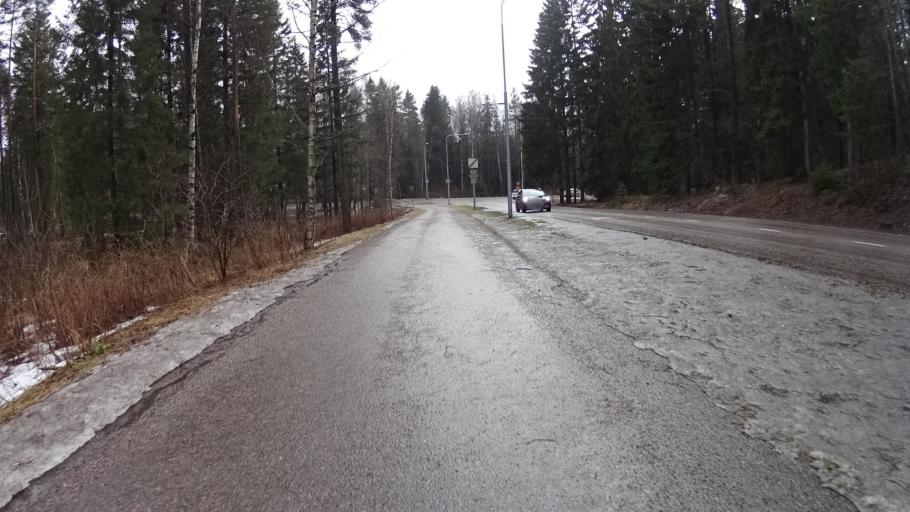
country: FI
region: Uusimaa
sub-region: Helsinki
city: Kilo
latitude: 60.2026
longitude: 24.7980
